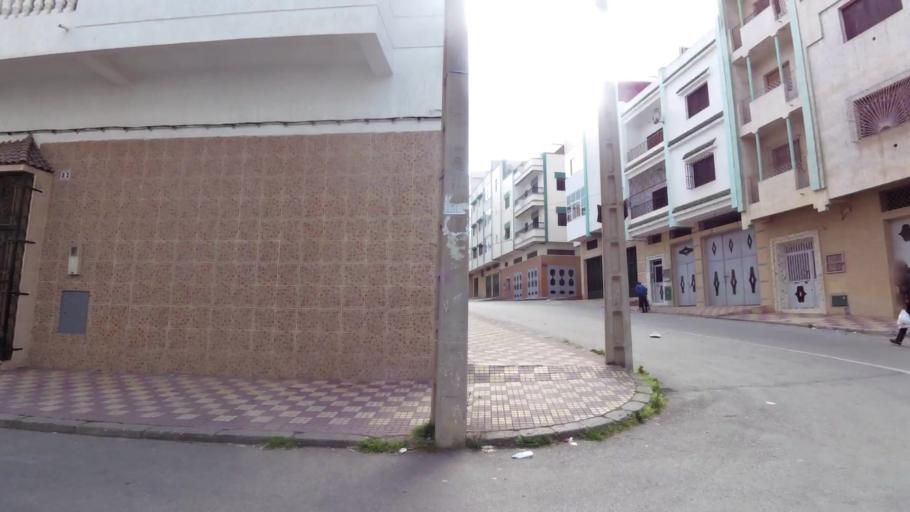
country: MA
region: Tanger-Tetouan
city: Tetouan
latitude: 35.5885
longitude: -5.3533
